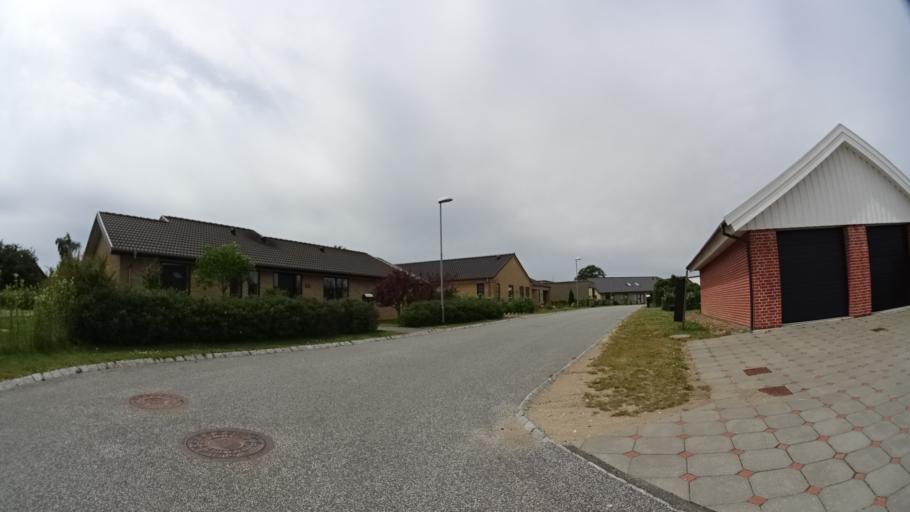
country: DK
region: Central Jutland
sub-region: Arhus Kommune
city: Stavtrup
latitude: 56.1204
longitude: 10.1264
